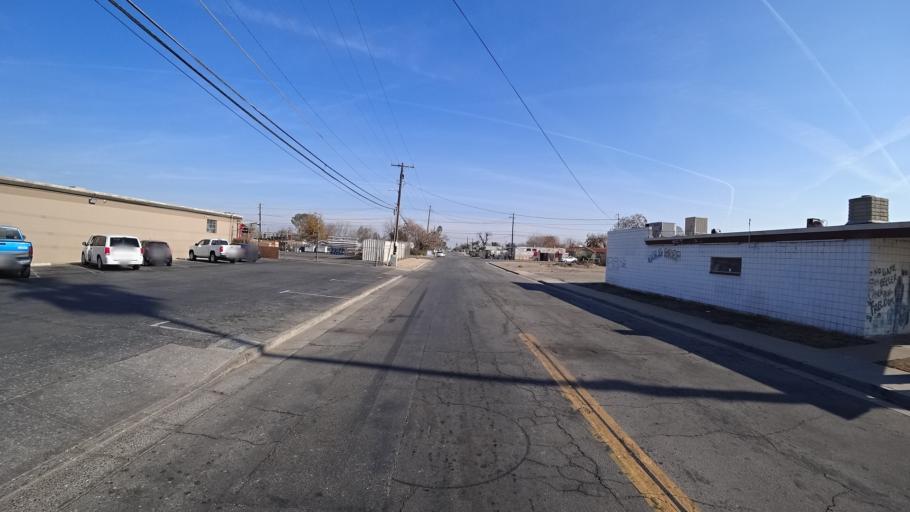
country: US
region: California
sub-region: Kern County
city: Bakersfield
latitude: 35.3358
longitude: -119.0160
